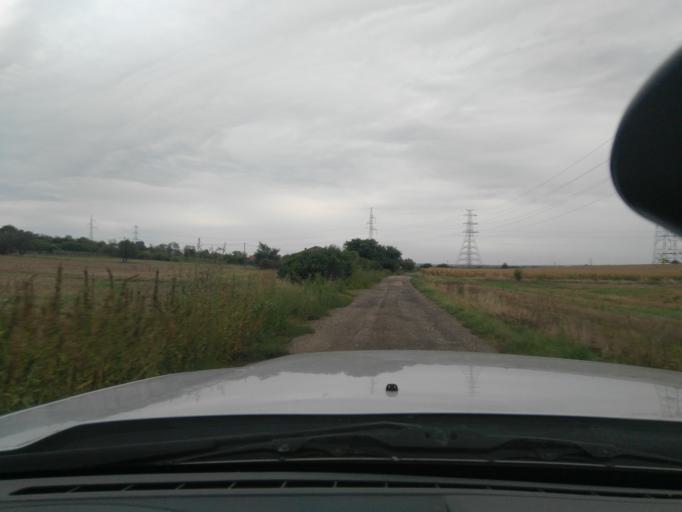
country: HU
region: Fejer
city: Martonvasar
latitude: 47.3517
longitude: 18.7639
